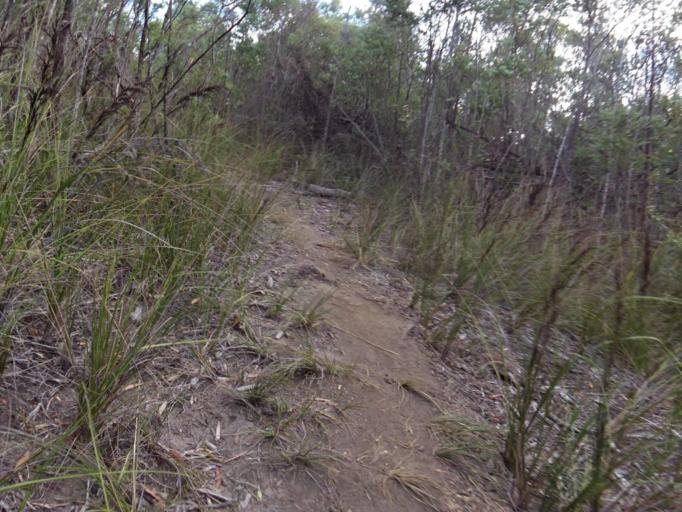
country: AU
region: Victoria
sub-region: Frankston
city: Frankston South
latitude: -38.1788
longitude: 145.1295
